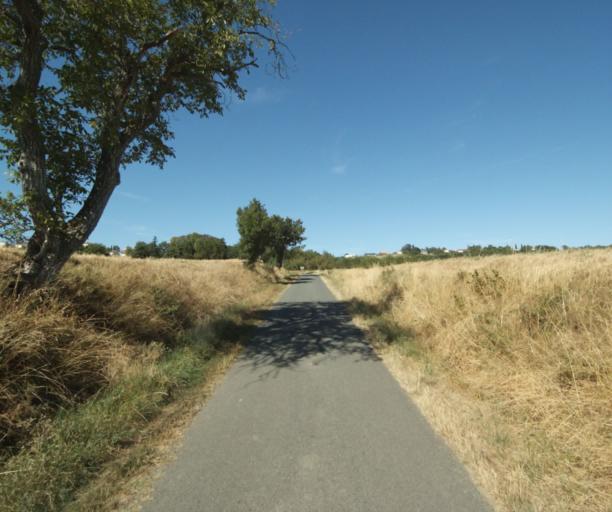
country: FR
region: Midi-Pyrenees
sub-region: Departement de la Haute-Garonne
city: Saint-Felix-Lauragais
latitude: 43.5140
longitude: 1.9104
